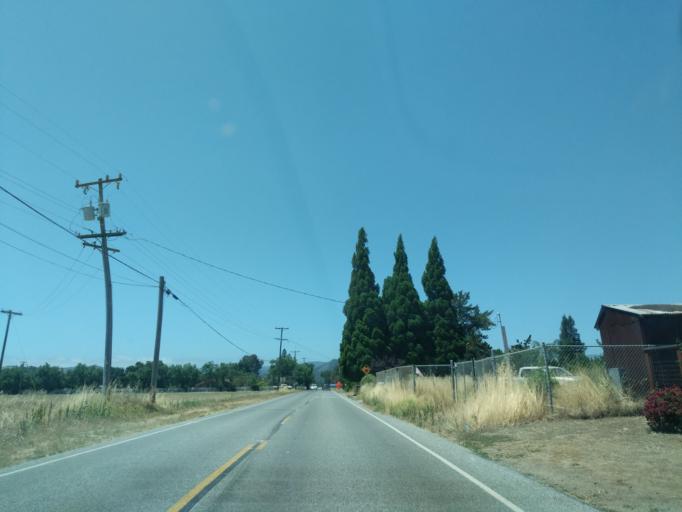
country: US
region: California
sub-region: Santa Clara County
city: San Martin
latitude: 37.1034
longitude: -121.6144
